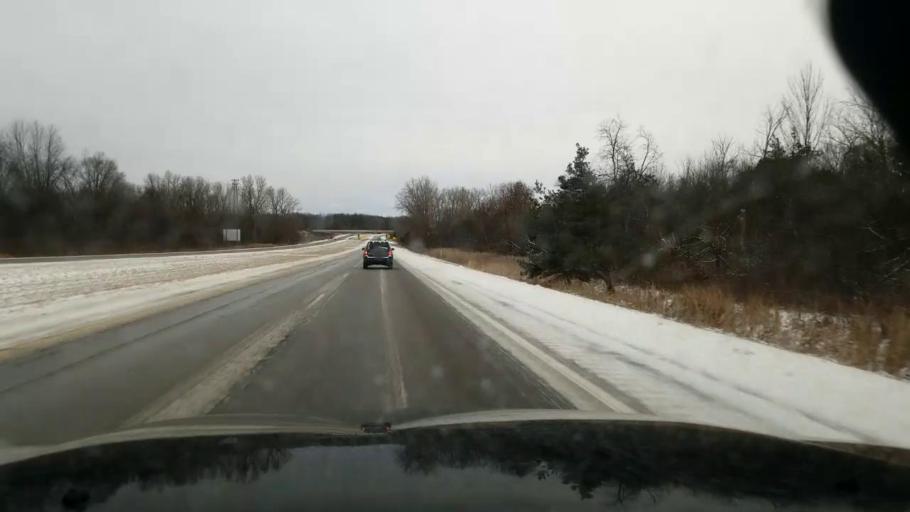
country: US
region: Michigan
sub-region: Jackson County
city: Jackson
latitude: 42.2377
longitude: -84.4755
